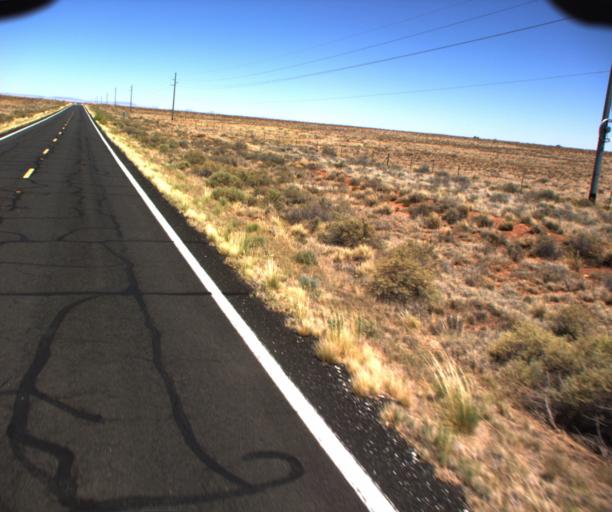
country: US
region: Arizona
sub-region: Coconino County
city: LeChee
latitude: 34.8958
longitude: -110.8606
